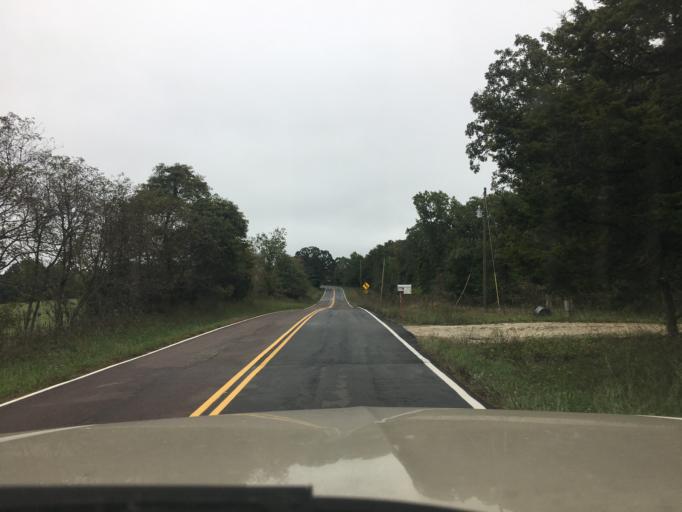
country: US
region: Missouri
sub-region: Crawford County
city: Cuba
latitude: 38.1895
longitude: -91.4828
